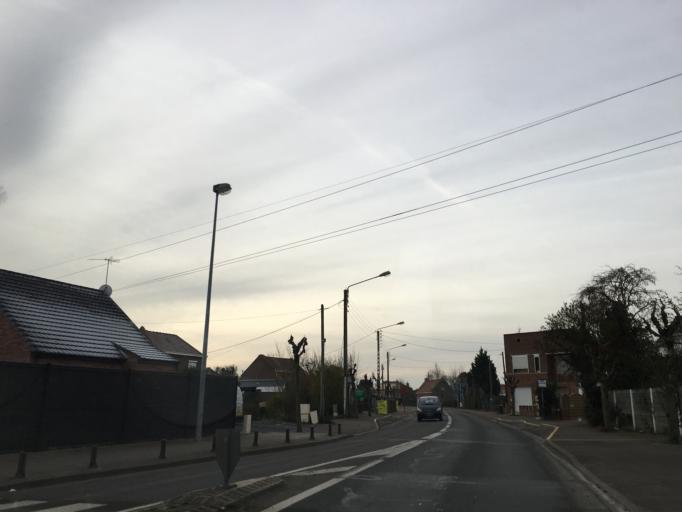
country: FR
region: Nord-Pas-de-Calais
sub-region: Departement du Pas-de-Calais
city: Courrieres
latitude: 50.4517
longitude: 2.9443
